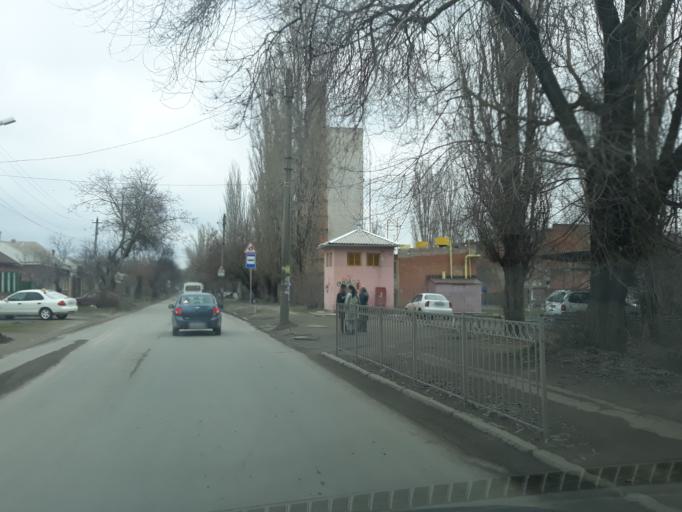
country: RU
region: Rostov
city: Taganrog
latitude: 47.2644
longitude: 38.9156
